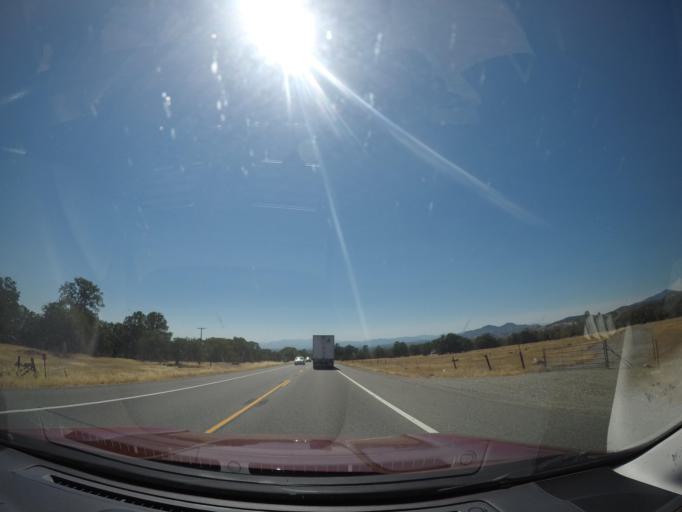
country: US
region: California
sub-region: Shasta County
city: Bella Vista
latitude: 40.6887
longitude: -122.1258
